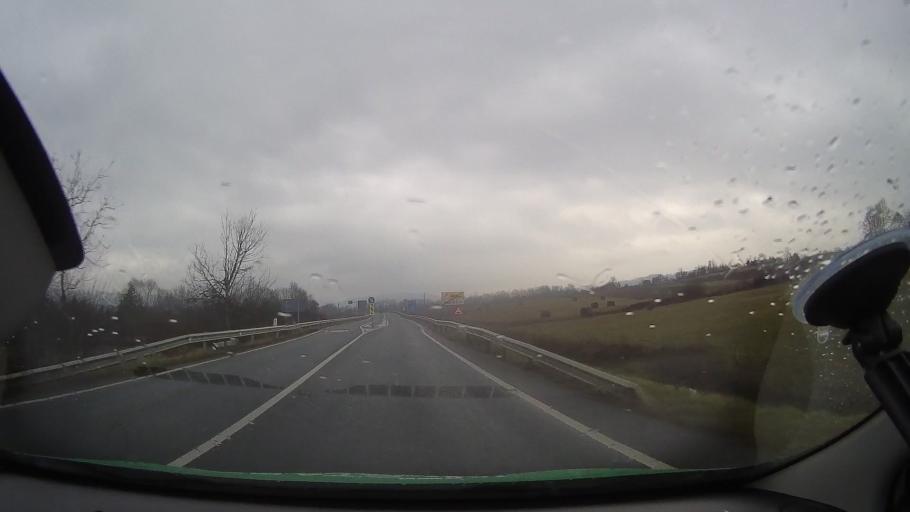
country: RO
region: Hunedoara
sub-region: Comuna Baia de Cris
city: Baia de Cris
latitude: 46.1707
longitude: 22.7184
